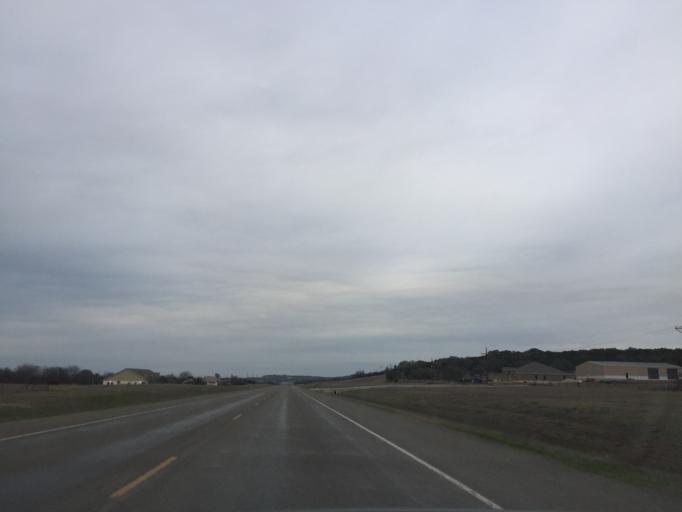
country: US
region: Texas
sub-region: Coryell County
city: Gatesville
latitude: 31.4497
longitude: -97.7151
